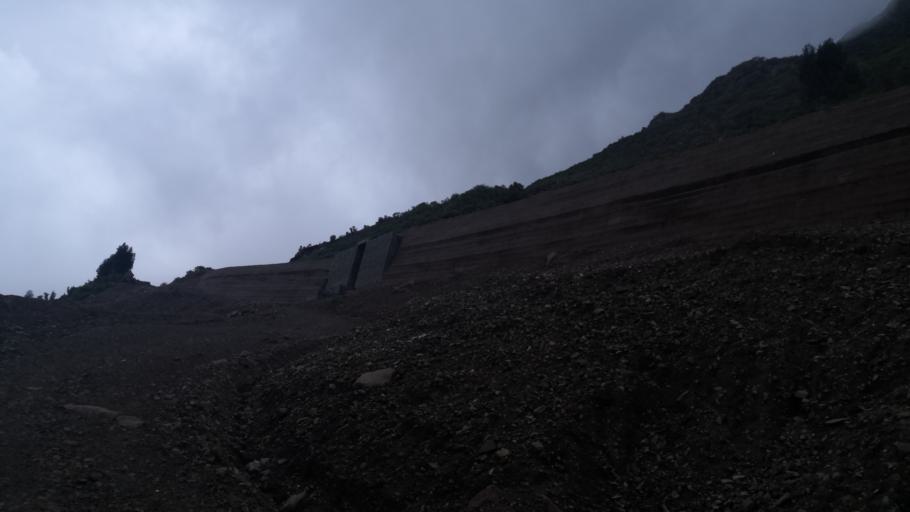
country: ET
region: Amhara
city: Kemise
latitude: 10.3374
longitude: 39.8201
